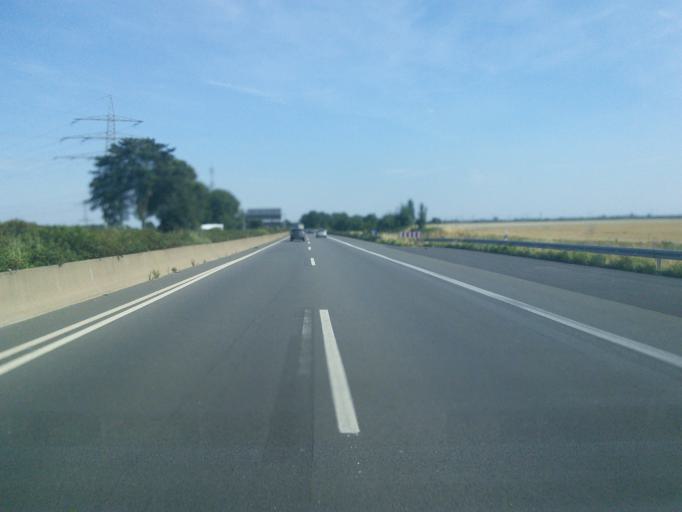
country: DE
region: North Rhine-Westphalia
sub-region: Regierungsbezirk Dusseldorf
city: Dusseldorf
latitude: 51.1462
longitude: 6.7629
